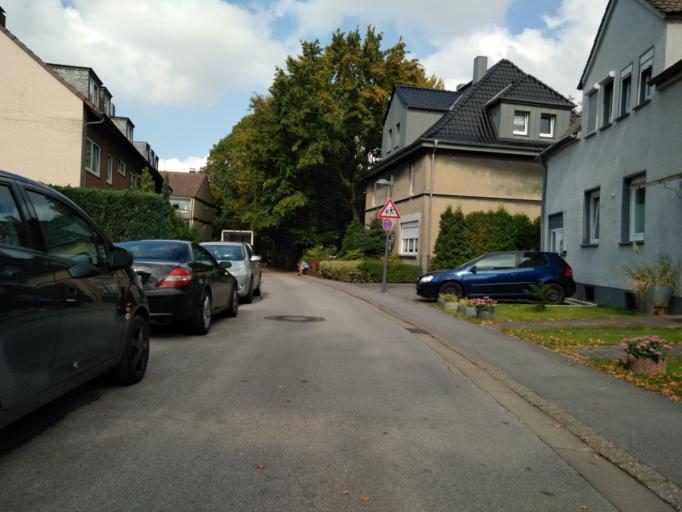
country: DE
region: North Rhine-Westphalia
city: Marl
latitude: 51.6044
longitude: 7.0508
